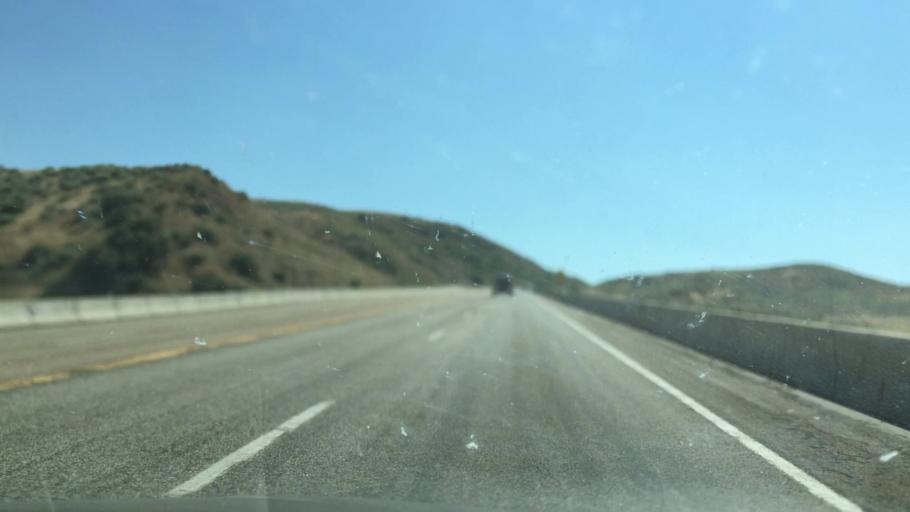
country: US
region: Idaho
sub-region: Ada County
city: Eagle
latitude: 43.8409
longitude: -116.2364
